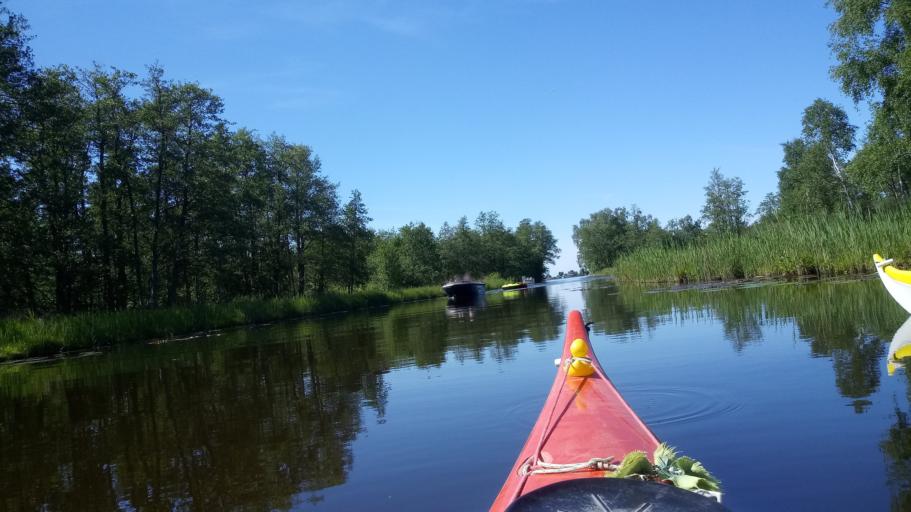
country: NL
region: South Holland
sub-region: Gemeente Nieuwkoop
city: Nieuwkoop
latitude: 52.1498
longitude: 4.8058
